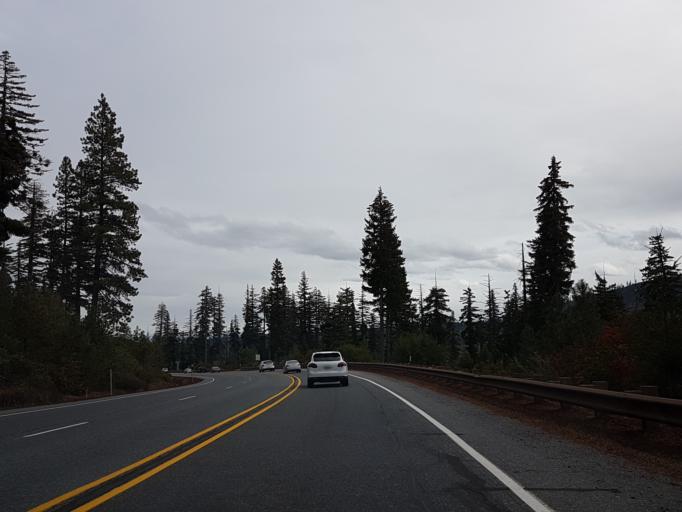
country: US
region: Oregon
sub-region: Deschutes County
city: Sisters
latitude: 44.4217
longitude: -121.7916
